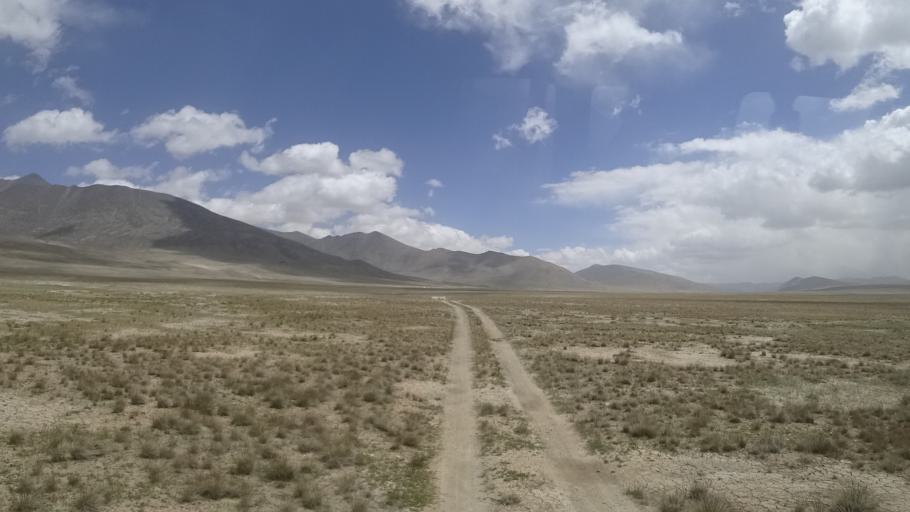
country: TJ
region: Gorno-Badakhshan
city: Murghob
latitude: 37.4805
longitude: 73.9803
